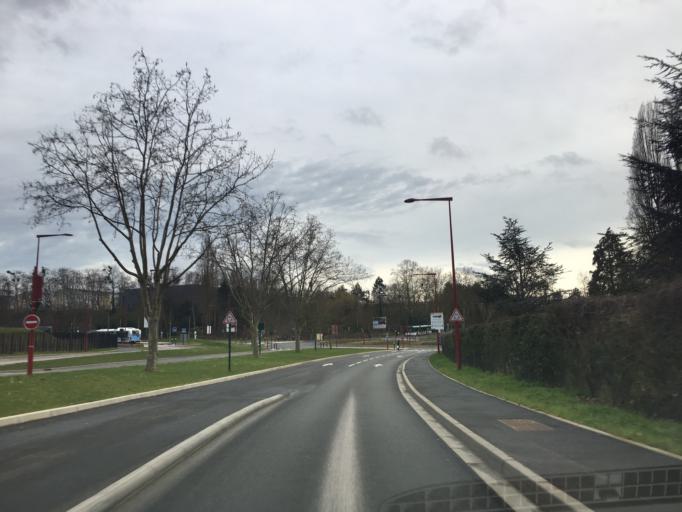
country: FR
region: Ile-de-France
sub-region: Departement du Val-d'Oise
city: Gonesse
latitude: 48.9865
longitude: 2.4596
